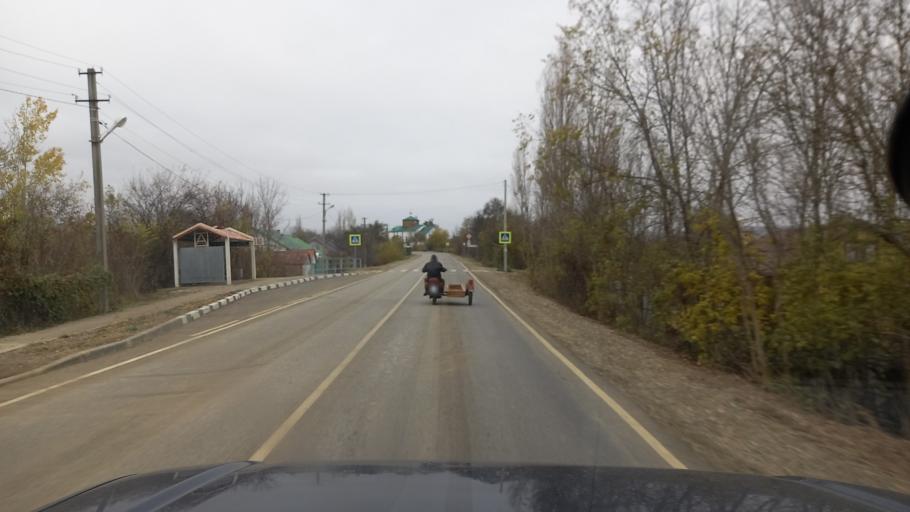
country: RU
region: Krasnodarskiy
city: Goryachiy Klyuch
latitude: 44.5213
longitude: 39.2926
